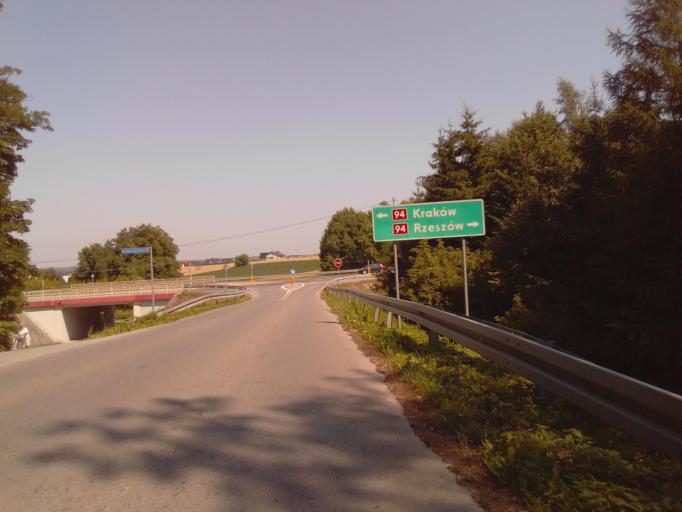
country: PL
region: Subcarpathian Voivodeship
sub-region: Powiat ropczycko-sedziszowski
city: Sedziszow Malopolski
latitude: 50.0669
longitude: 21.6631
